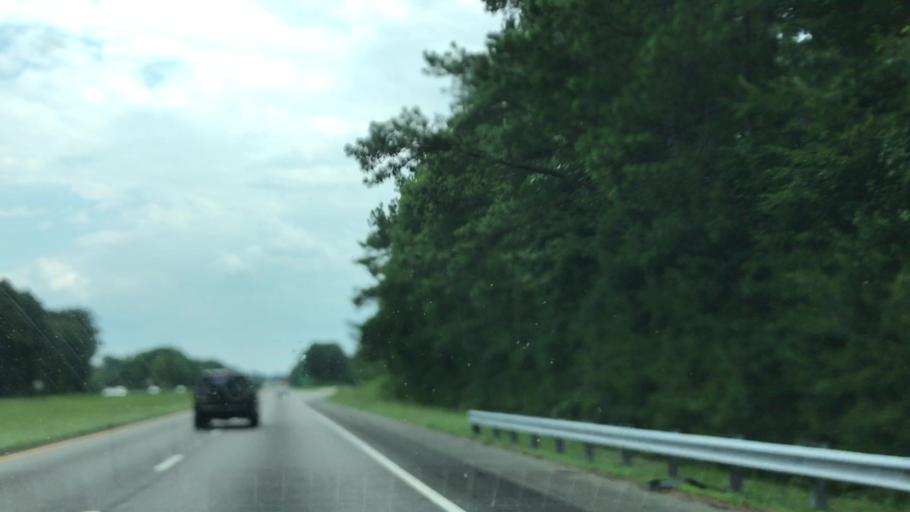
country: US
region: South Carolina
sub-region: Richland County
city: Blythewood
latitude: 34.2901
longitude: -80.9973
